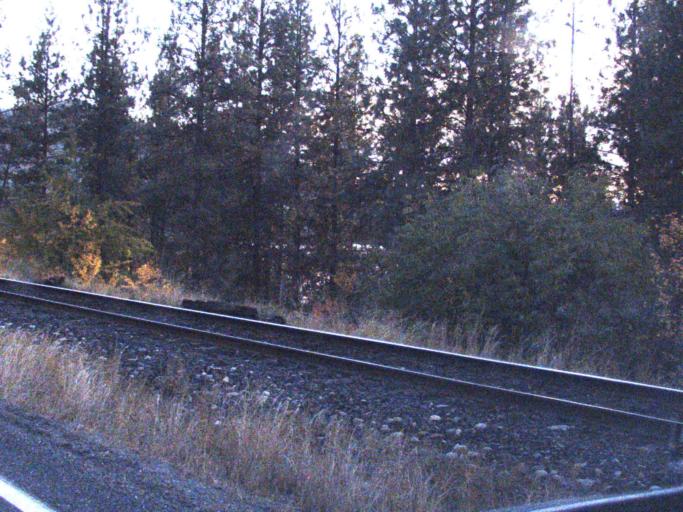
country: US
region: Washington
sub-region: Stevens County
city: Kettle Falls
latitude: 48.6976
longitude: -118.0139
